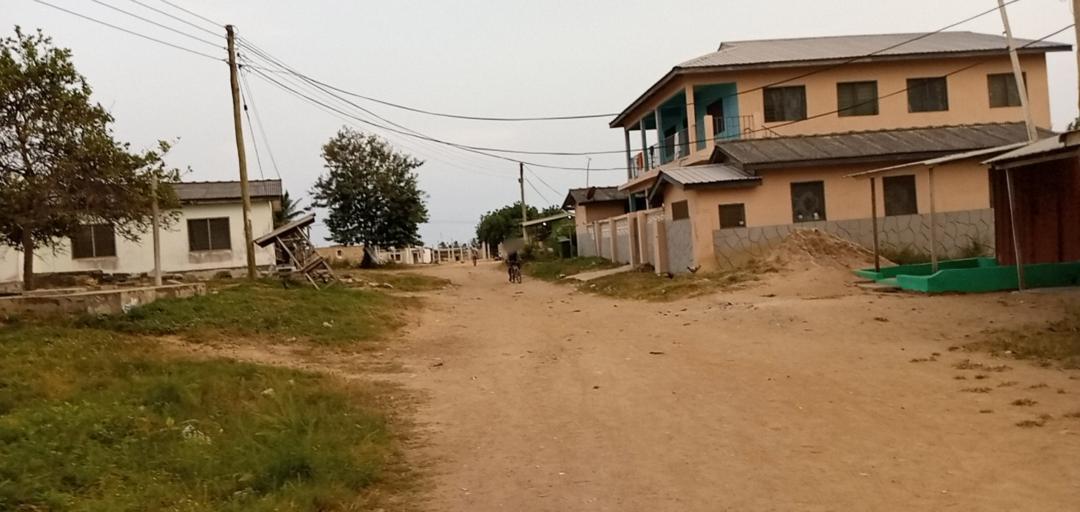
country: GH
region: Central
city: Winneba
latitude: 5.3555
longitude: -0.6294
